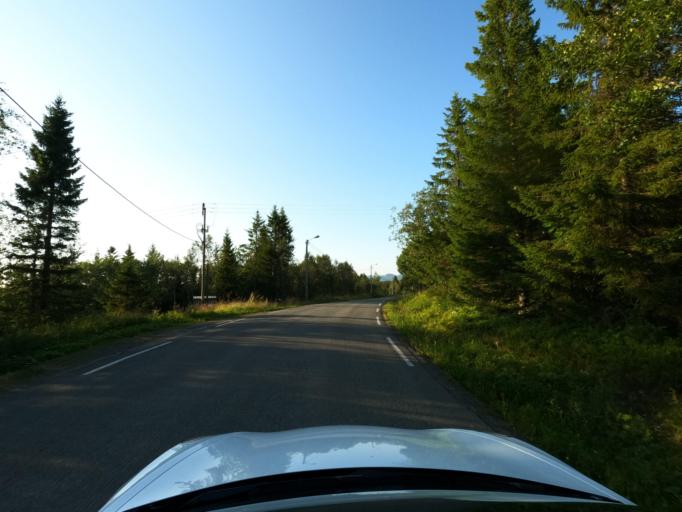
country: NO
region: Nordland
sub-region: Ballangen
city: Ballangen
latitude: 68.4950
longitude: 16.7344
